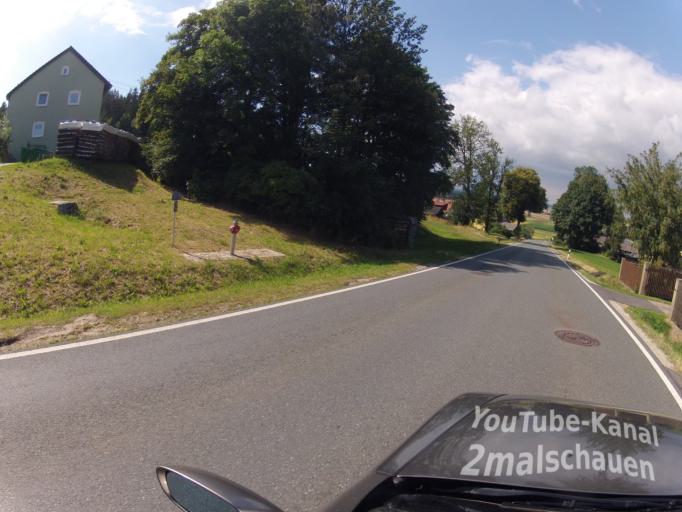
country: DE
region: Bavaria
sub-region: Upper Franconia
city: Roslau
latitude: 50.0683
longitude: 11.9749
